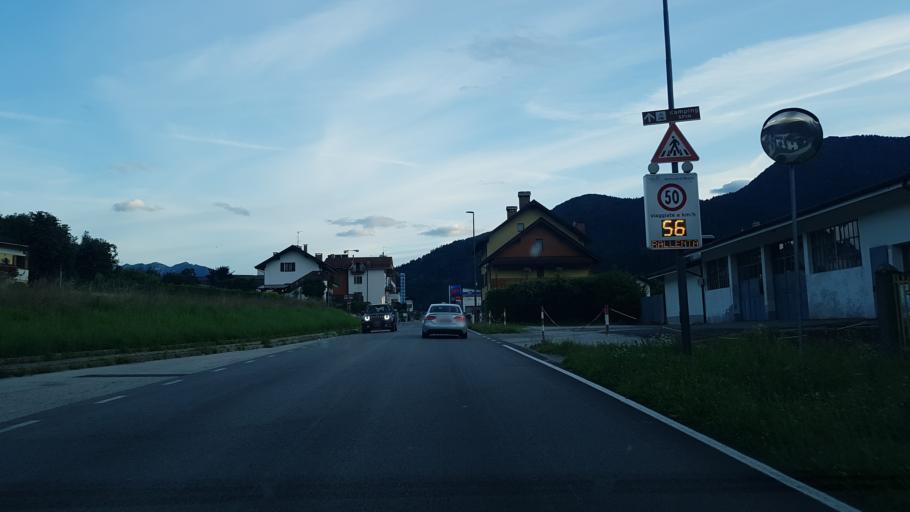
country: IT
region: Friuli Venezia Giulia
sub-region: Provincia di Udine
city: Ovaro
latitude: 46.4896
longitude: 12.8652
